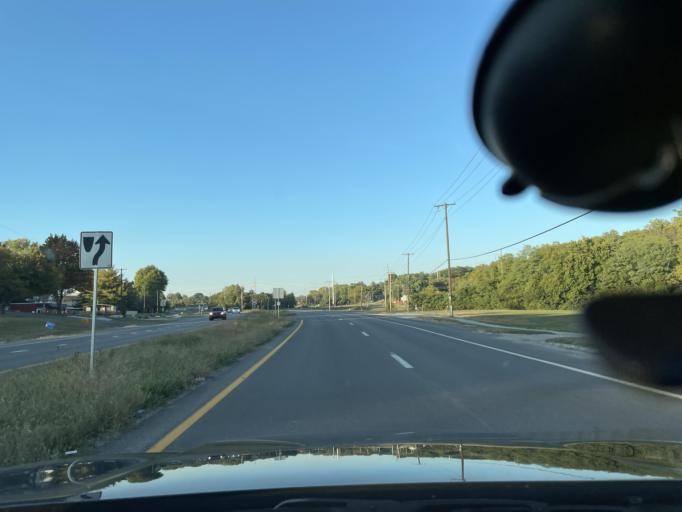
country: US
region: Missouri
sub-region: Andrew County
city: Country Club Village
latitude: 39.8037
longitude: -94.8420
